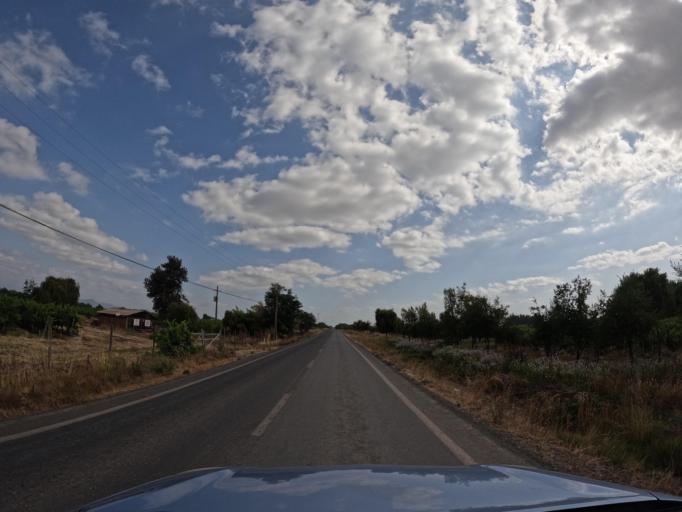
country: CL
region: Maule
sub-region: Provincia de Curico
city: Molina
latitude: -35.1762
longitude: -71.2932
